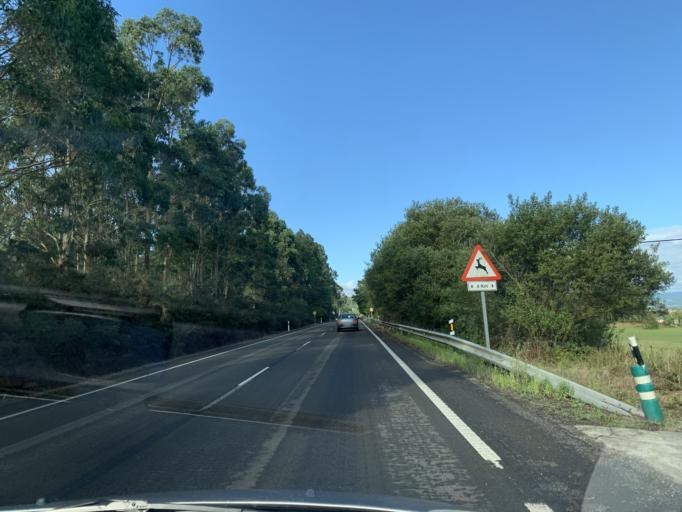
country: ES
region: Galicia
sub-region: Provincia de Lugo
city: Barreiros
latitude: 43.5444
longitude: -7.1634
